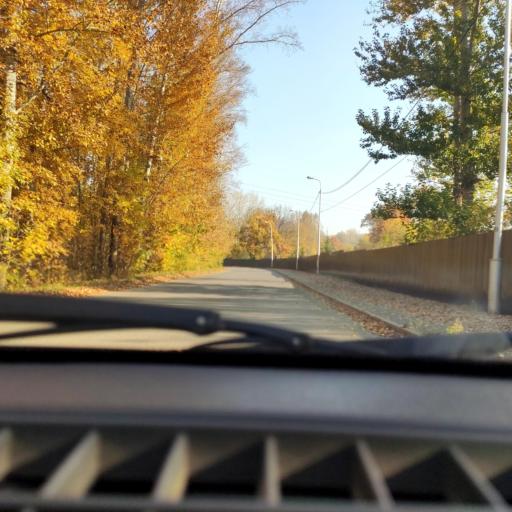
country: RU
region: Bashkortostan
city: Ufa
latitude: 54.8100
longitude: 56.0394
